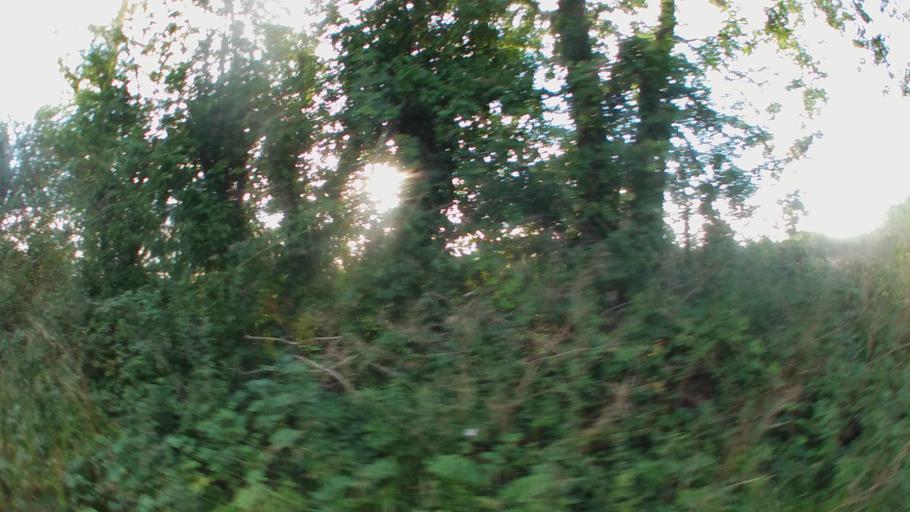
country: IE
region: Leinster
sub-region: Kilkenny
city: Kilkenny
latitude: 52.6788
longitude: -7.2223
